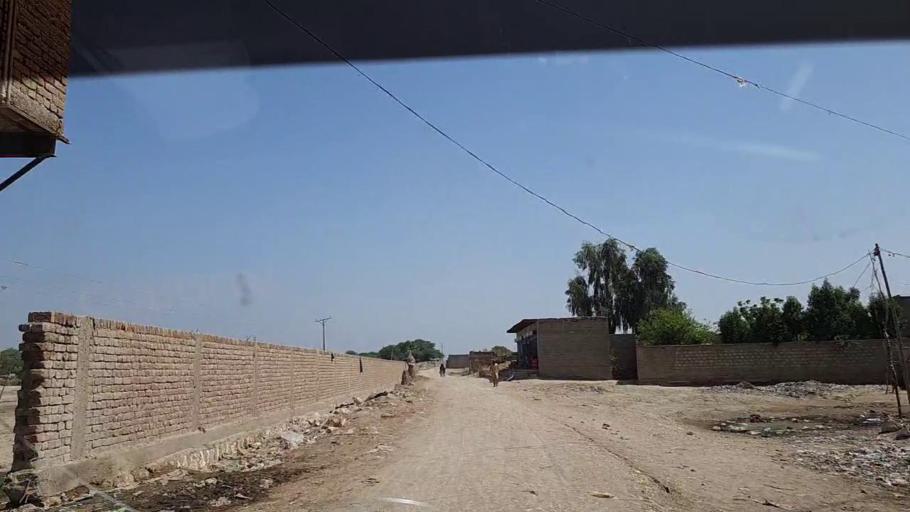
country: PK
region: Sindh
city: Ghauspur
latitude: 28.1366
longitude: 69.0835
